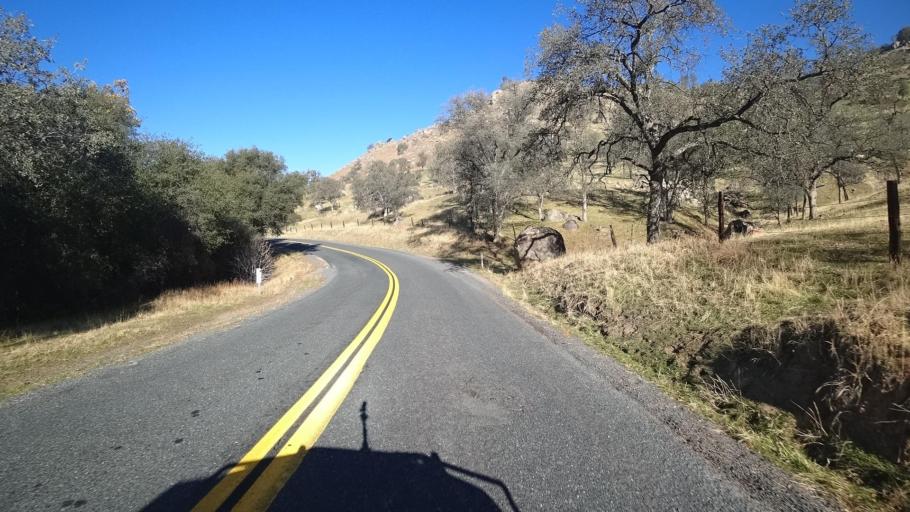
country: US
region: California
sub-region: Kern County
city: Alta Sierra
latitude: 35.7913
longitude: -118.8050
